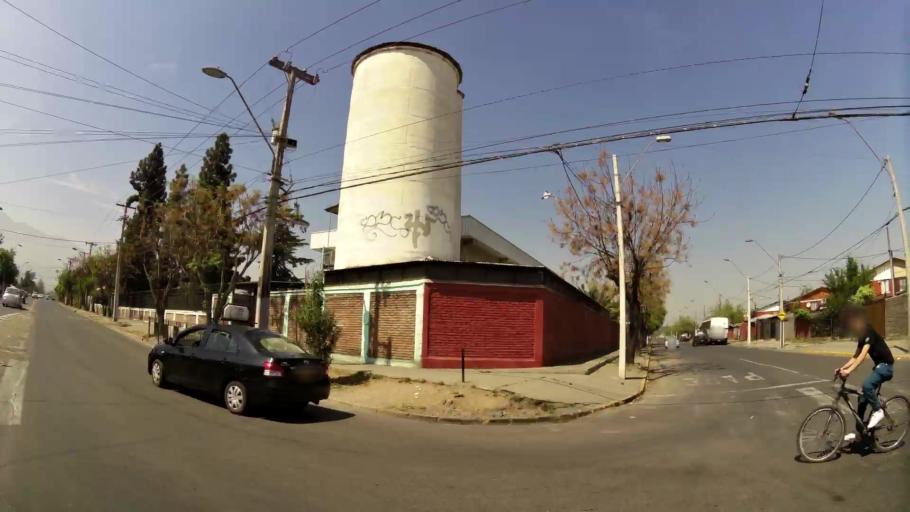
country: CL
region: Santiago Metropolitan
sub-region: Provincia de Santiago
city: La Pintana
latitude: -33.5541
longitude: -70.6073
